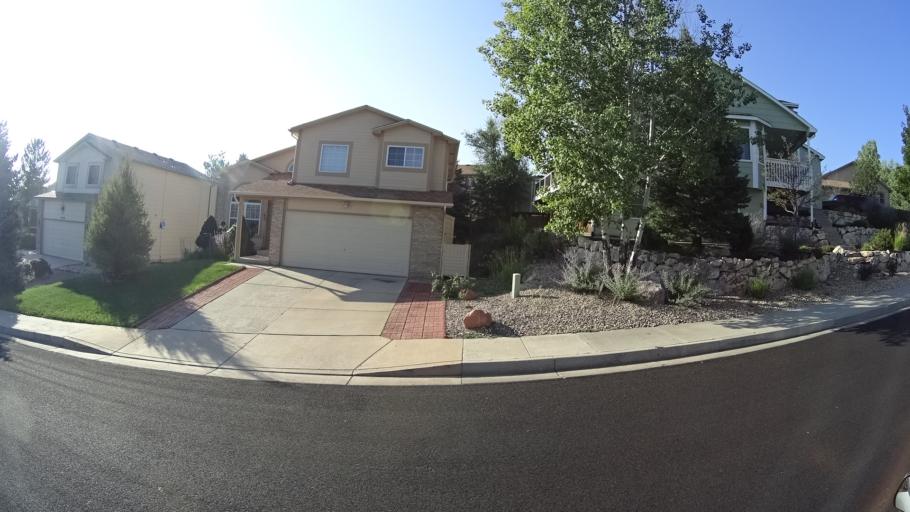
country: US
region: Colorado
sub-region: El Paso County
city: Colorado Springs
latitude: 38.8896
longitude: -104.8519
